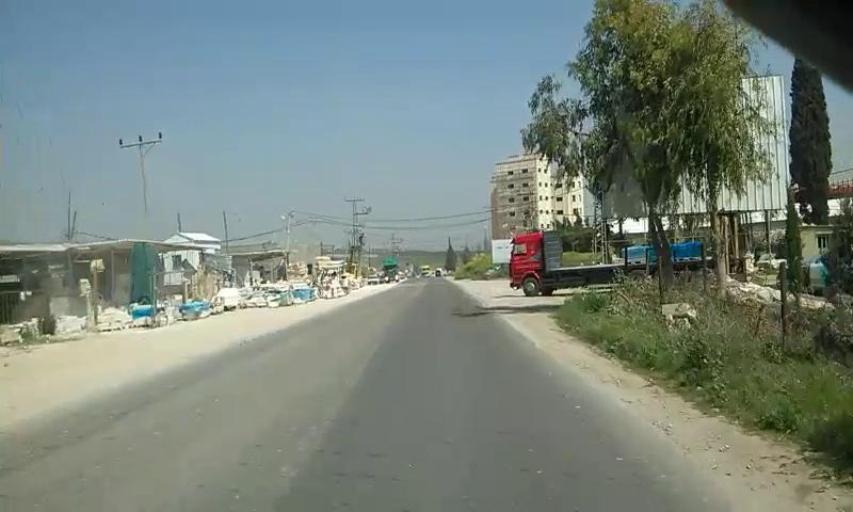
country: PS
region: West Bank
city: Ash Shuhada'
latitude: 32.4338
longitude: 35.2698
